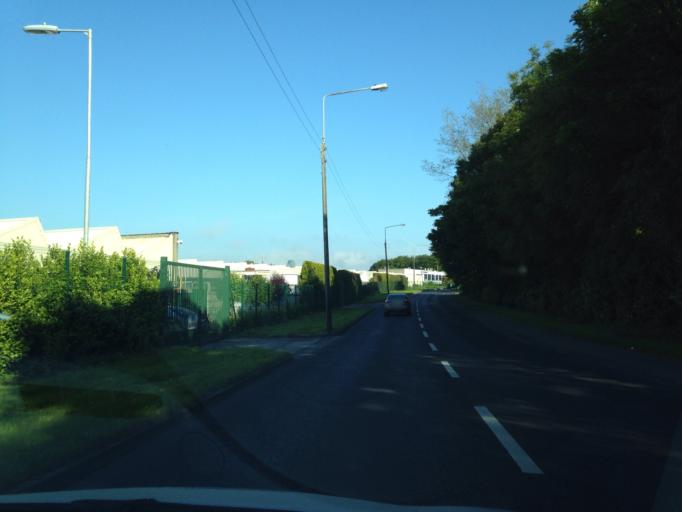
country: IE
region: Connaught
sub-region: County Galway
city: Gaillimh
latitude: 53.2845
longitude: -9.0205
